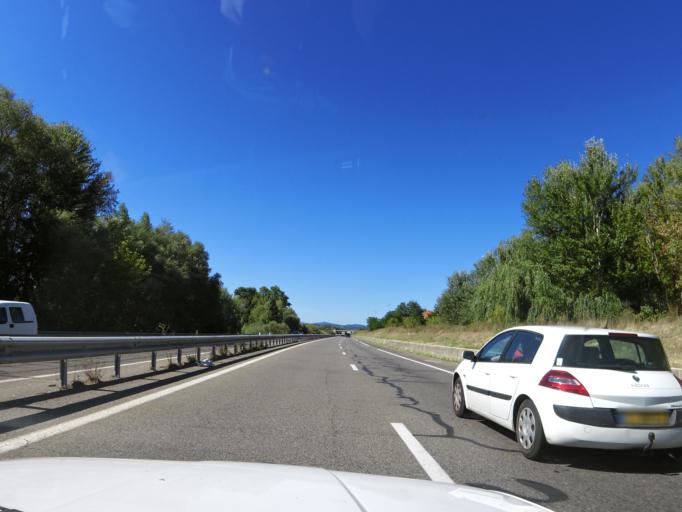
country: FR
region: Languedoc-Roussillon
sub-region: Departement du Gard
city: Saint-Hilaire-de-Brethmas
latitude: 44.0872
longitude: 4.1081
